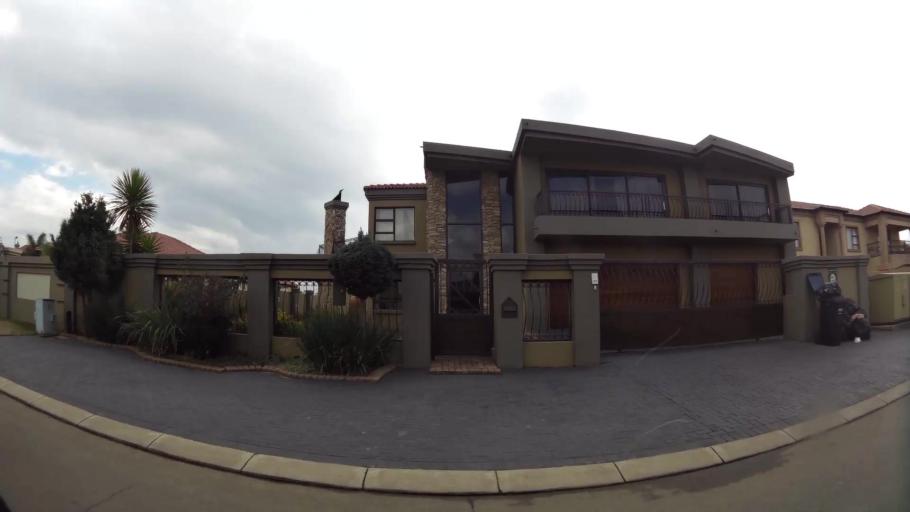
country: ZA
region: Gauteng
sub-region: Sedibeng District Municipality
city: Vanderbijlpark
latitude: -26.7283
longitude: 27.8681
